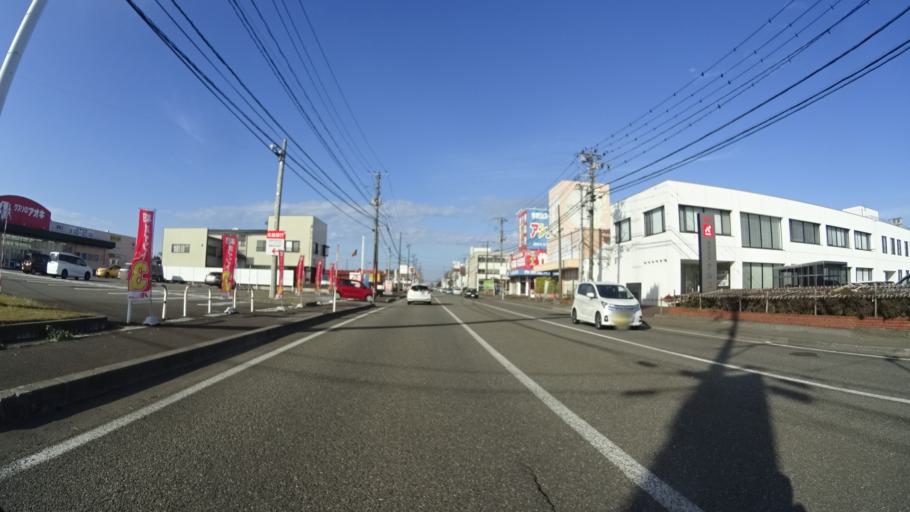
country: JP
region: Niigata
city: Joetsu
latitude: 37.1367
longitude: 138.2413
